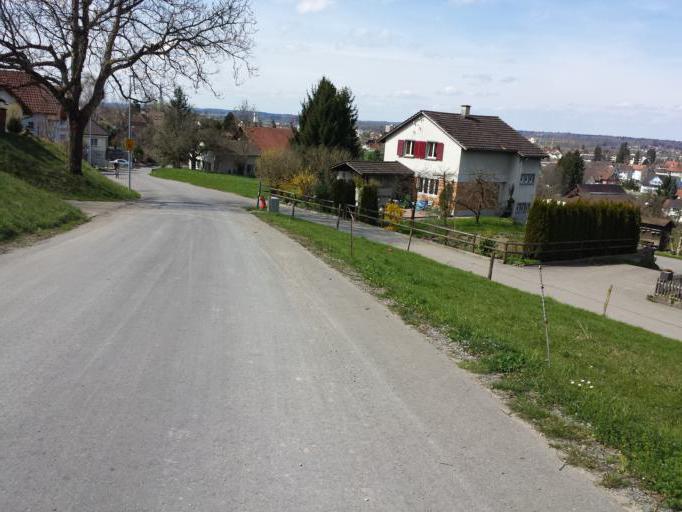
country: CH
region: Thurgau
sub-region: Arbon District
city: Amriswil
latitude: 47.5392
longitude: 9.3103
